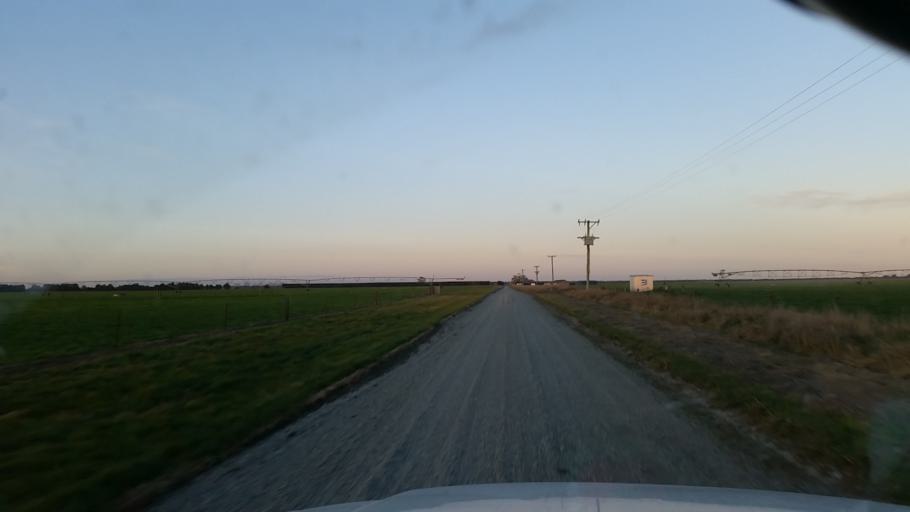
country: NZ
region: Canterbury
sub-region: Ashburton District
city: Tinwald
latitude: -43.9533
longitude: 171.5603
